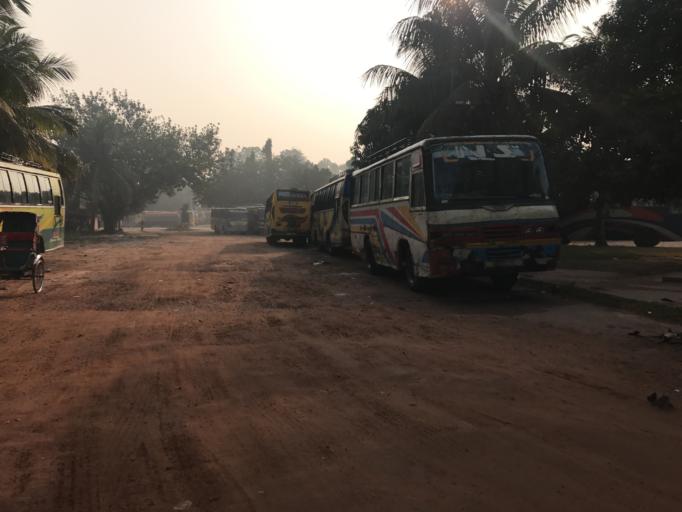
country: BD
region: Khulna
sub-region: Magura
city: Magura
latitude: 23.4976
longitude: 89.4323
